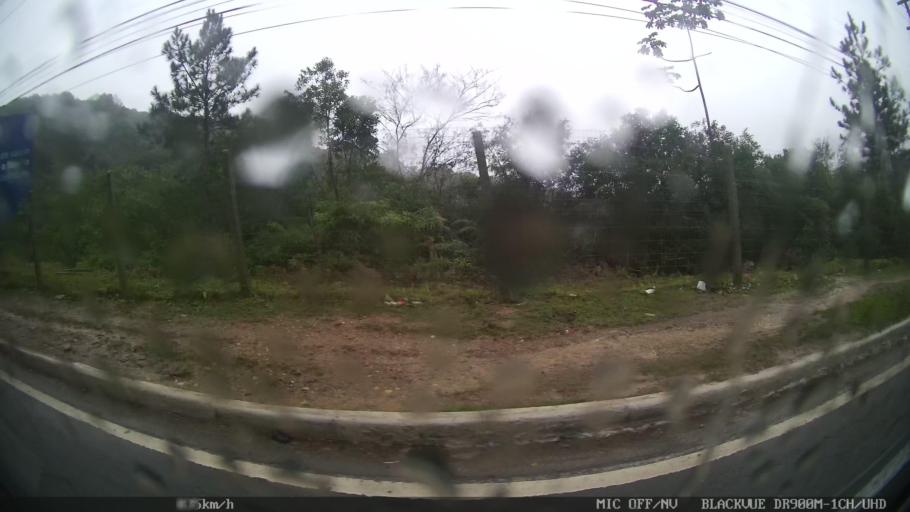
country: BR
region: Santa Catarina
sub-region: Itajai
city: Itajai
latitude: -26.9380
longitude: -48.6410
